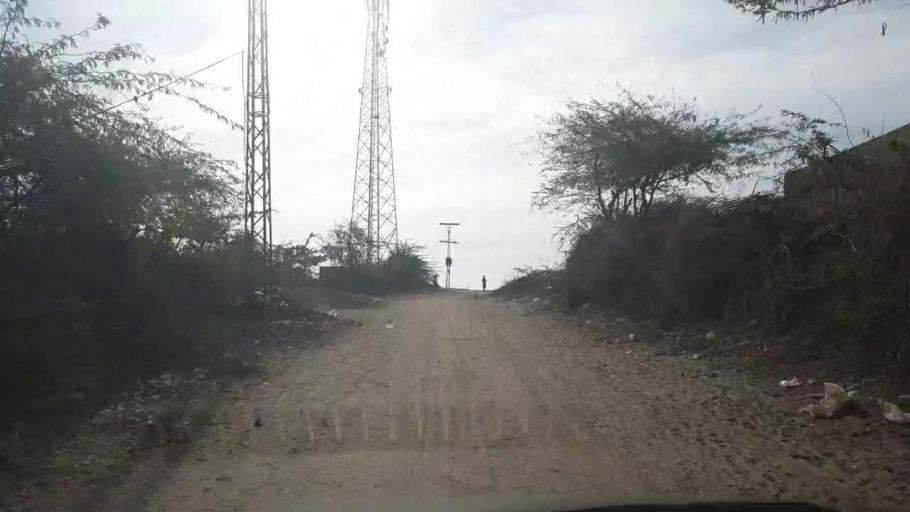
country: PK
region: Sindh
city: Umarkot
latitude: 25.3097
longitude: 69.7061
